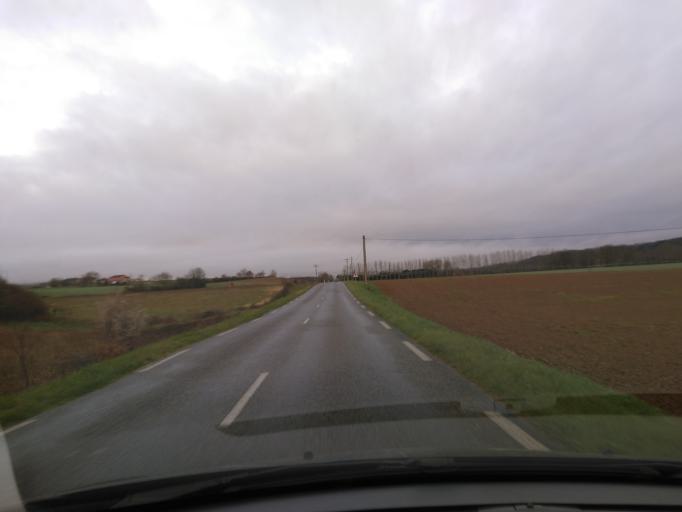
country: FR
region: Midi-Pyrenees
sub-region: Departement de la Haute-Garonne
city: Montesquieu-Volvestre
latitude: 43.1513
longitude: 1.2949
